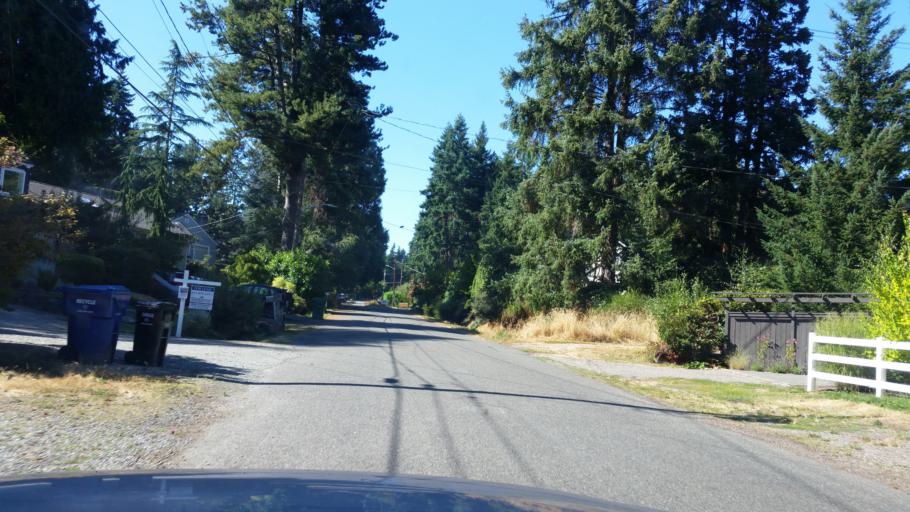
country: US
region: Washington
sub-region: King County
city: Shoreline
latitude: 47.7315
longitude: -122.3572
